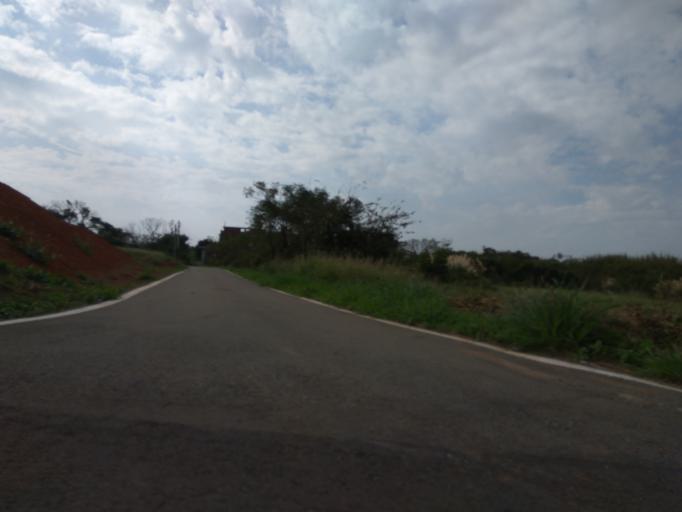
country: TW
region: Taiwan
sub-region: Hsinchu
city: Zhubei
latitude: 24.9684
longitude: 121.0169
